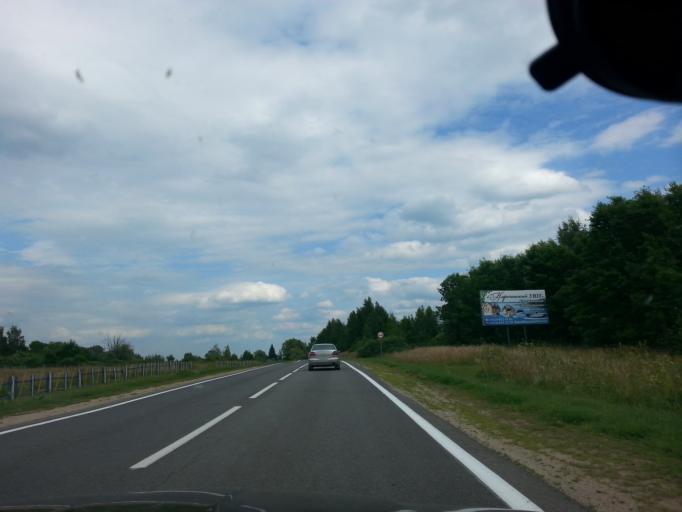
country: BY
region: Minsk
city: Myadzyel
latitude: 54.8804
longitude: 26.8575
